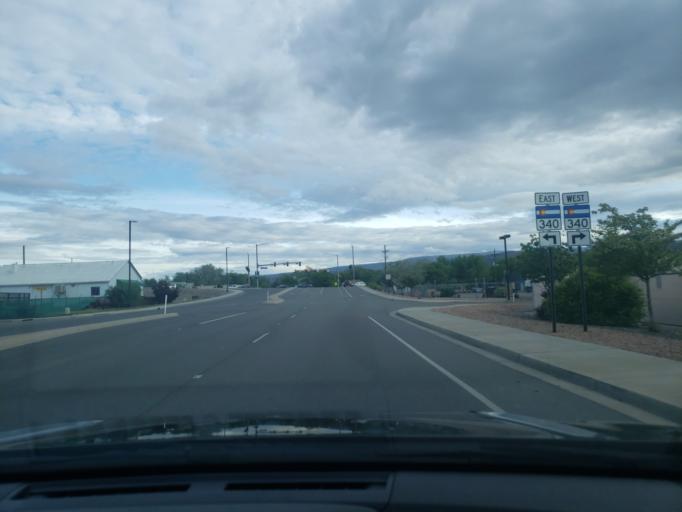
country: US
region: Colorado
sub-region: Mesa County
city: Grand Junction
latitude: 39.0696
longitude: -108.5793
